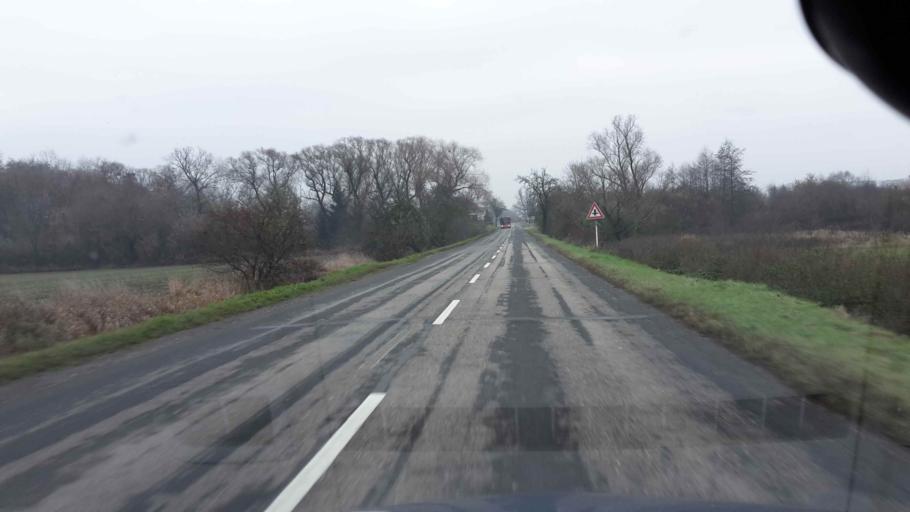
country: CZ
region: Olomoucky
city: Horka nad Moravou
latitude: 49.6083
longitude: 17.2102
